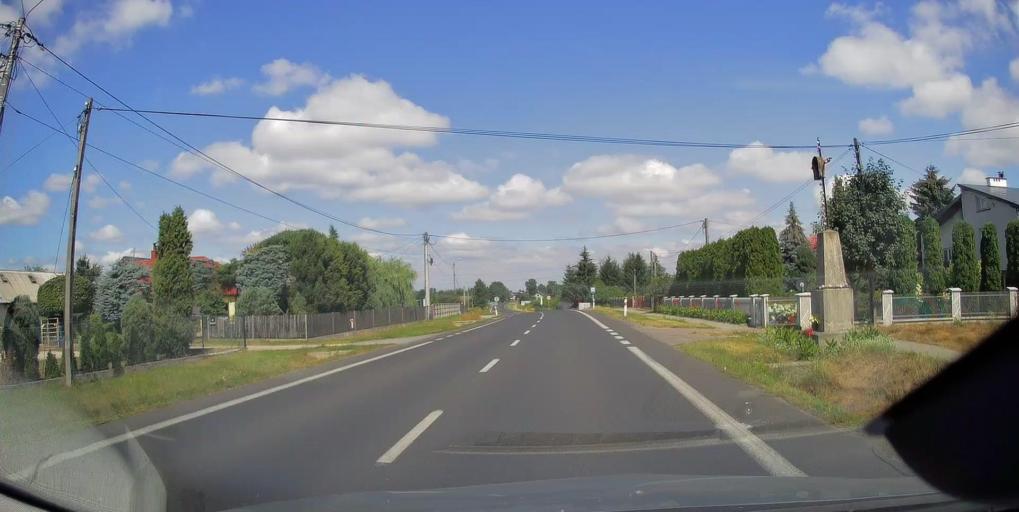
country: PL
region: Subcarpathian Voivodeship
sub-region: Powiat debicki
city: Brzeznica
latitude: 50.1213
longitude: 21.4883
